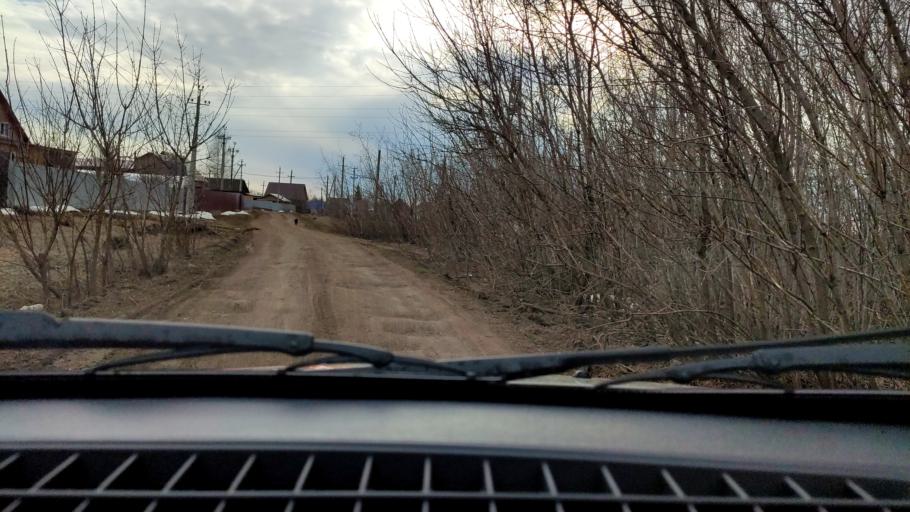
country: RU
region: Bashkortostan
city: Iglino
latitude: 54.8272
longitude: 56.4160
